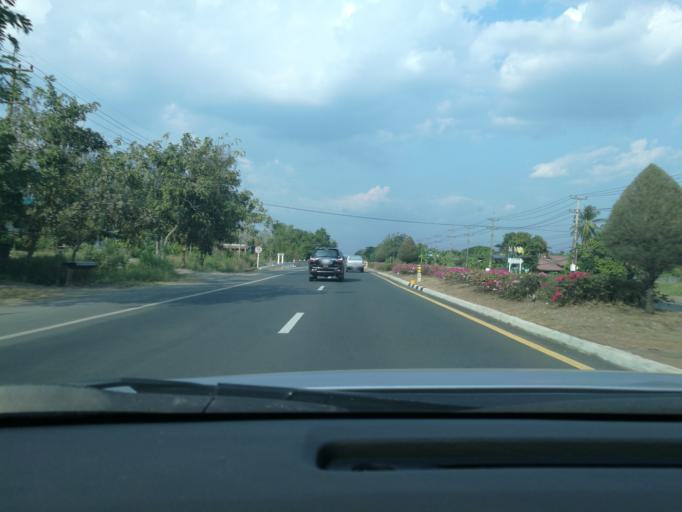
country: TH
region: Phetchabun
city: Phetchabun
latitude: 16.2882
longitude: 101.0637
